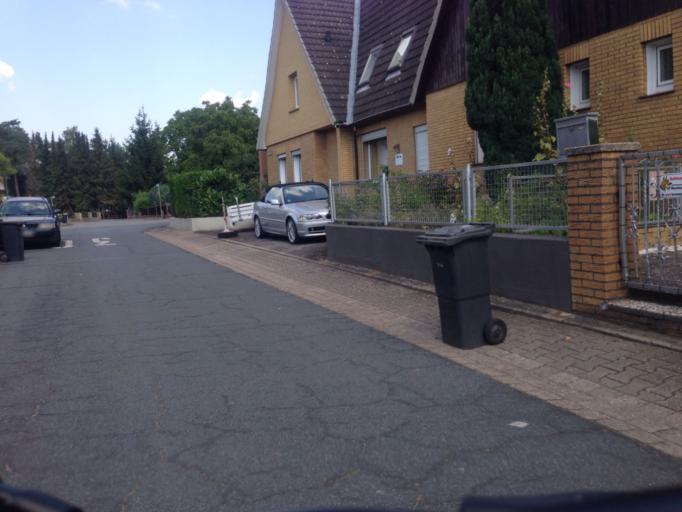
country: DE
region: Lower Saxony
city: Adendorf
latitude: 53.2839
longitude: 10.4348
